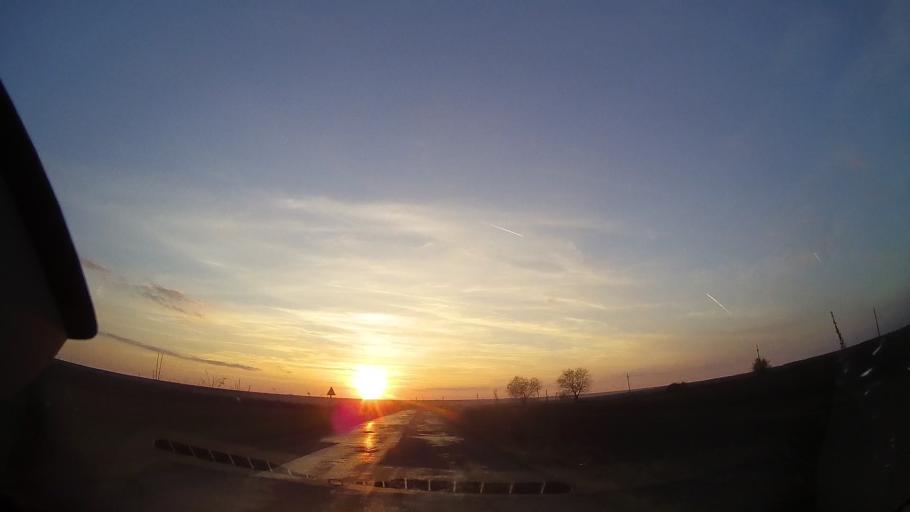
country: RO
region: Constanta
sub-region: Comuna Mereni
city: Mereni
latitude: 44.0199
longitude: 28.3481
